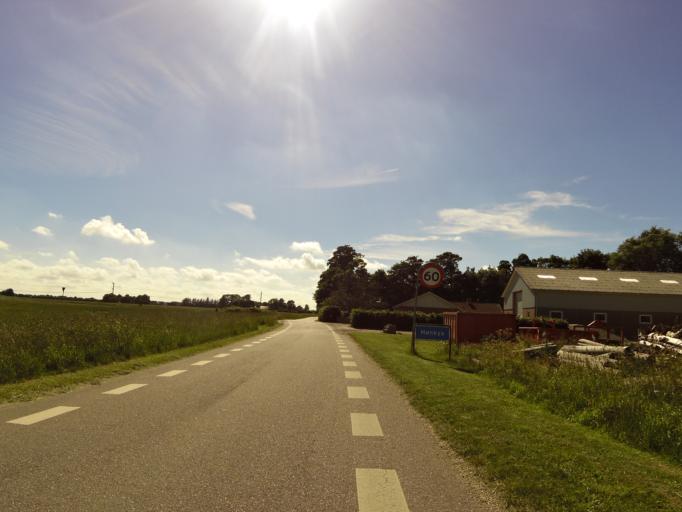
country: DK
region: South Denmark
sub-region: Aabenraa Kommune
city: Rodekro
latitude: 55.0664
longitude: 9.2640
